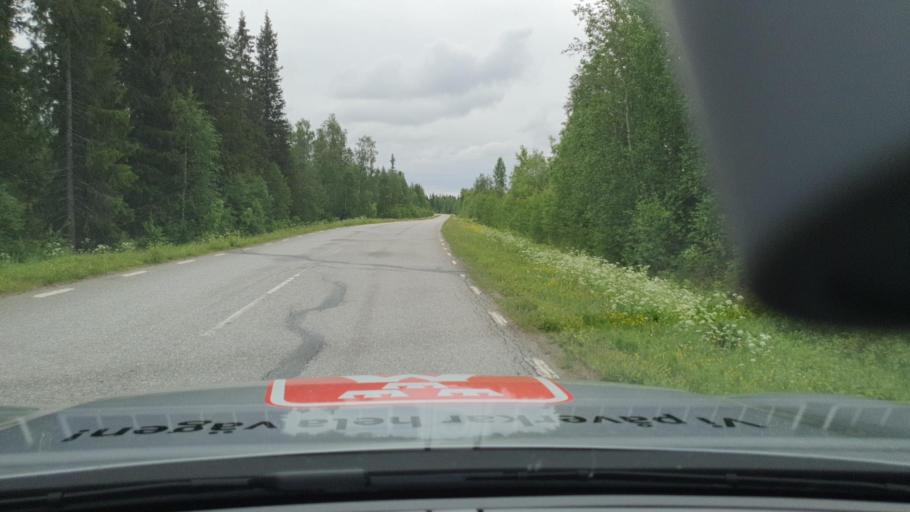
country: SE
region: Norrbotten
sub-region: Lulea Kommun
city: Ranea
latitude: 65.8611
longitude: 22.2351
